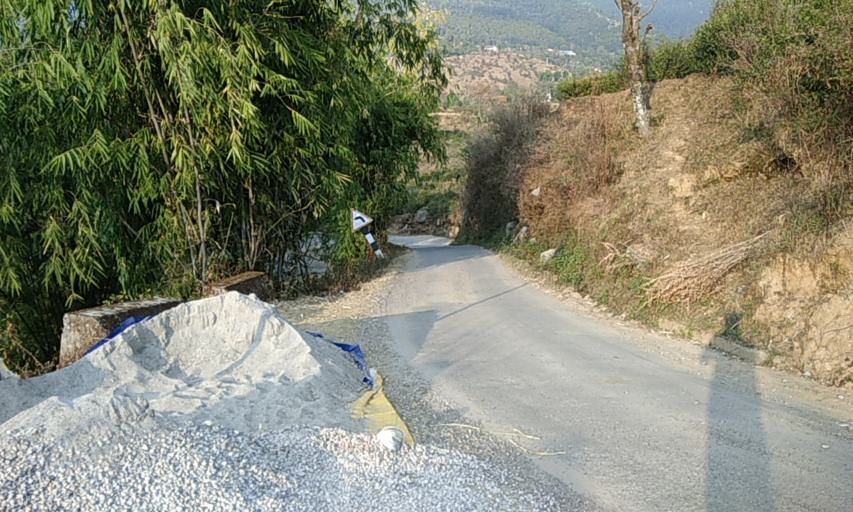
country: IN
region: Himachal Pradesh
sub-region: Kangra
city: Palampur
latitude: 32.1151
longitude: 76.5780
